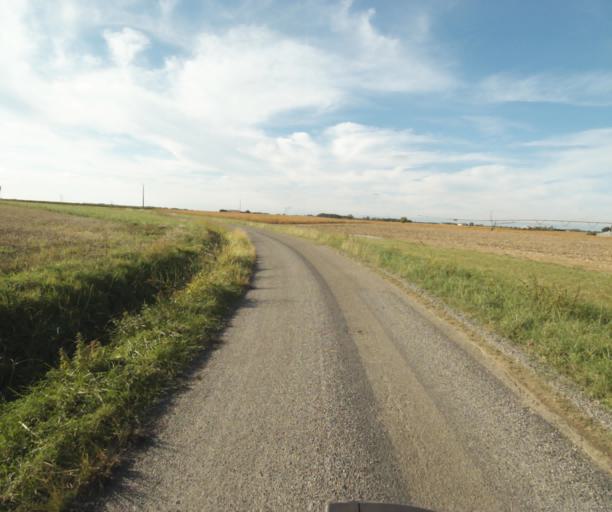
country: FR
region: Midi-Pyrenees
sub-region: Departement du Tarn-et-Garonne
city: Finhan
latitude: 43.9046
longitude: 1.1327
